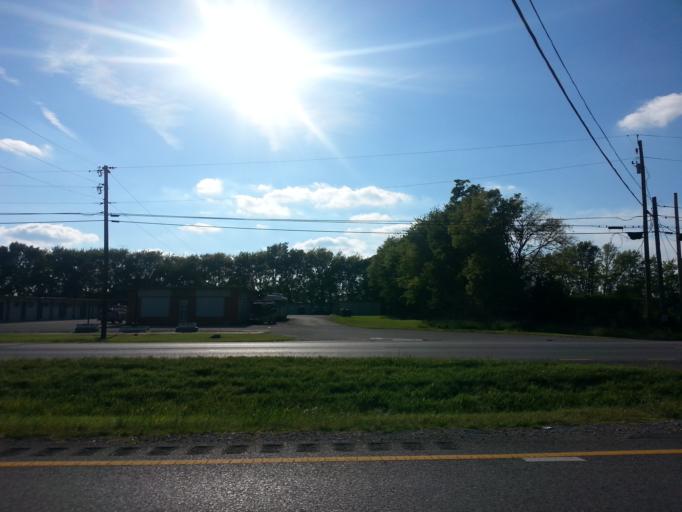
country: US
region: Alabama
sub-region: Colbert County
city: Muscle Shoals
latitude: 34.7203
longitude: -87.6679
